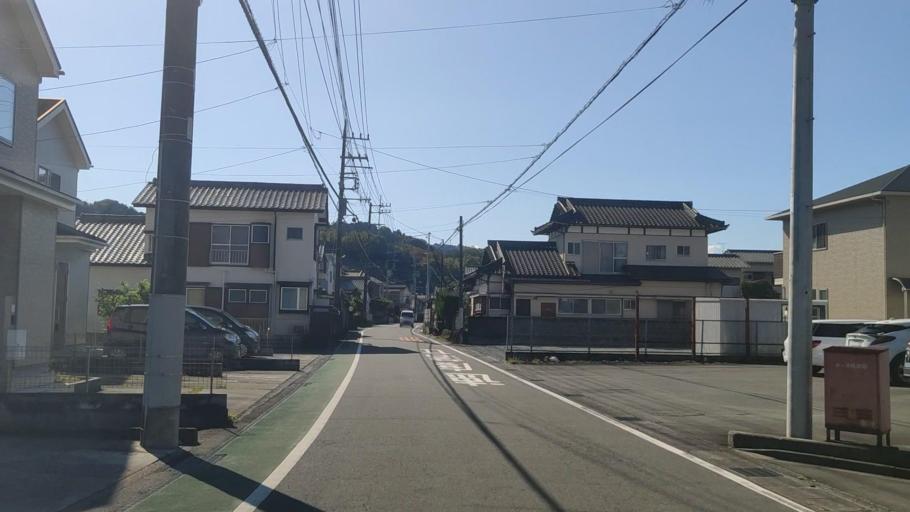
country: JP
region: Shizuoka
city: Mishima
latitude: 35.0029
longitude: 138.9434
